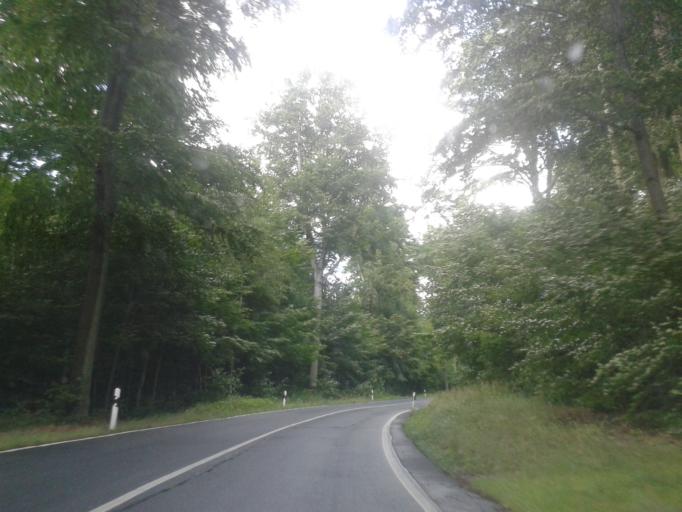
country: DE
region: Saxony
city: Radeberg
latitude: 51.0836
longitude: 13.9021
